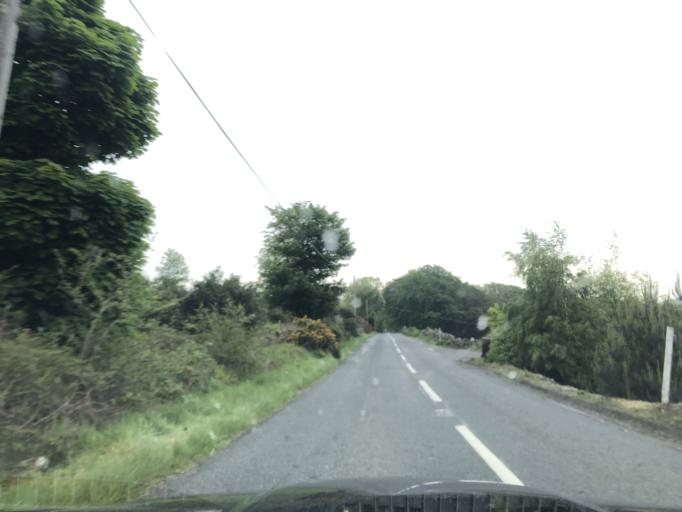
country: GB
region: Northern Ireland
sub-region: Down District
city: Castlewellan
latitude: 54.2229
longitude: -5.9711
